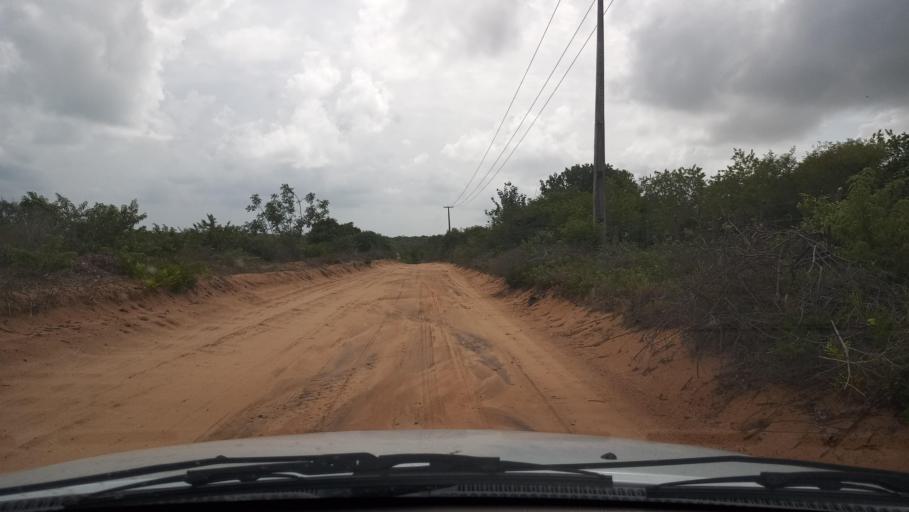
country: BR
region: Rio Grande do Norte
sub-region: Maxaranguape
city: Sao Miguel
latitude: -5.4839
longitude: -35.3083
